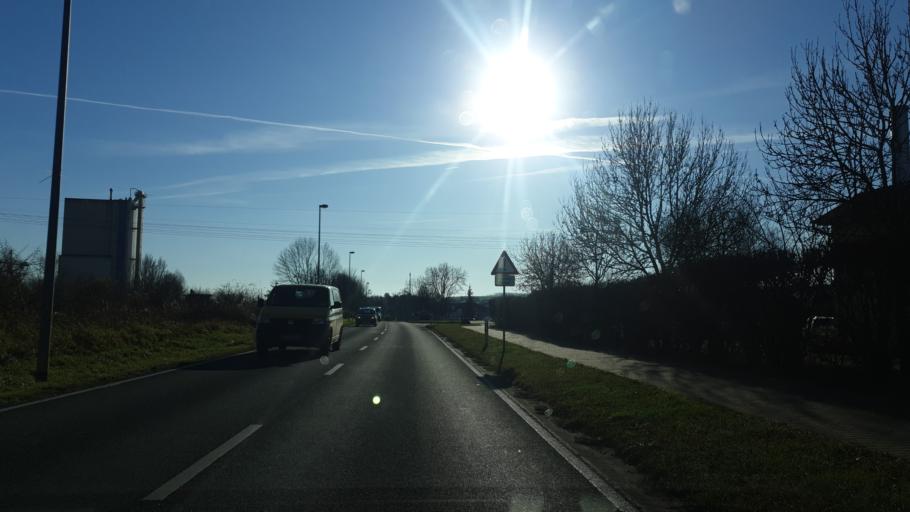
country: DE
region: Thuringia
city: Hartmannsdorf
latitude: 50.9715
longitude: 11.9820
